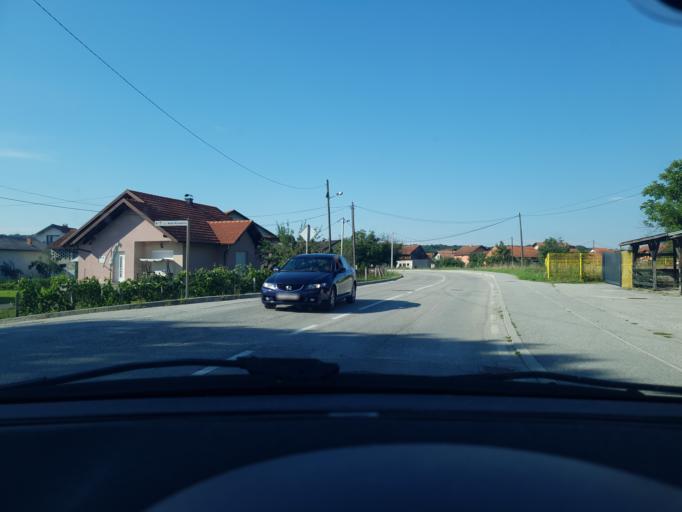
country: HR
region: Zagrebacka
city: Jablanovec
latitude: 45.9046
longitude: 15.8537
